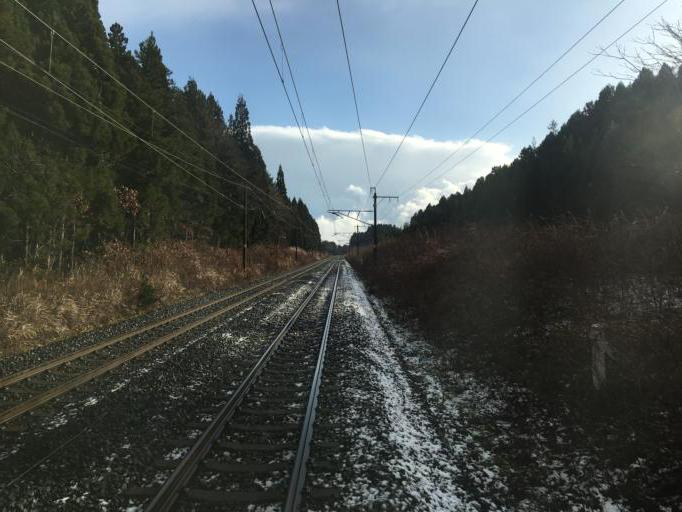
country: JP
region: Aomori
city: Aomori Shi
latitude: 40.9097
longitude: 141.0528
